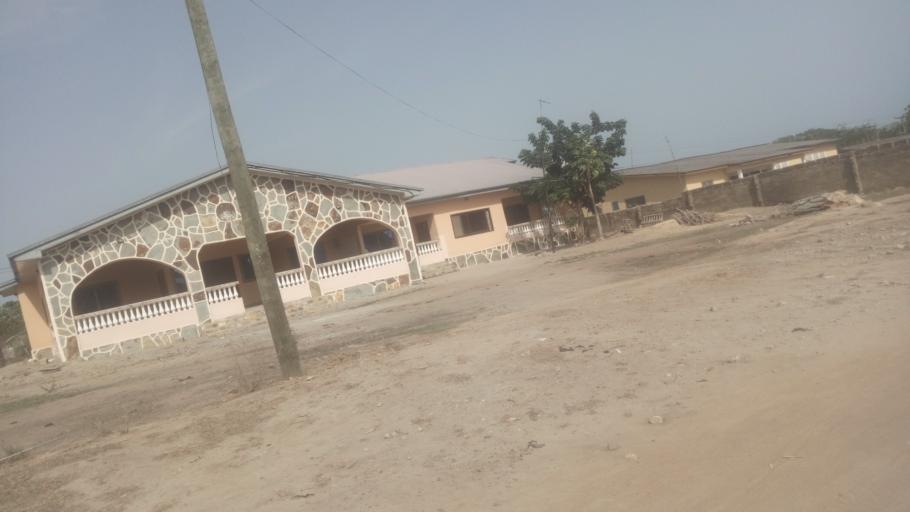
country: GH
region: Central
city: Winneba
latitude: 5.3796
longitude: -0.6429
